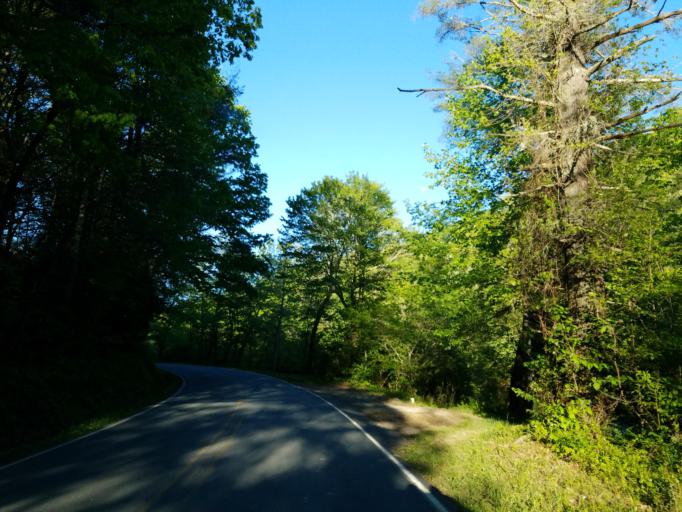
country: US
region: Georgia
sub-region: Fannin County
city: Blue Ridge
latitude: 34.7576
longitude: -84.2064
